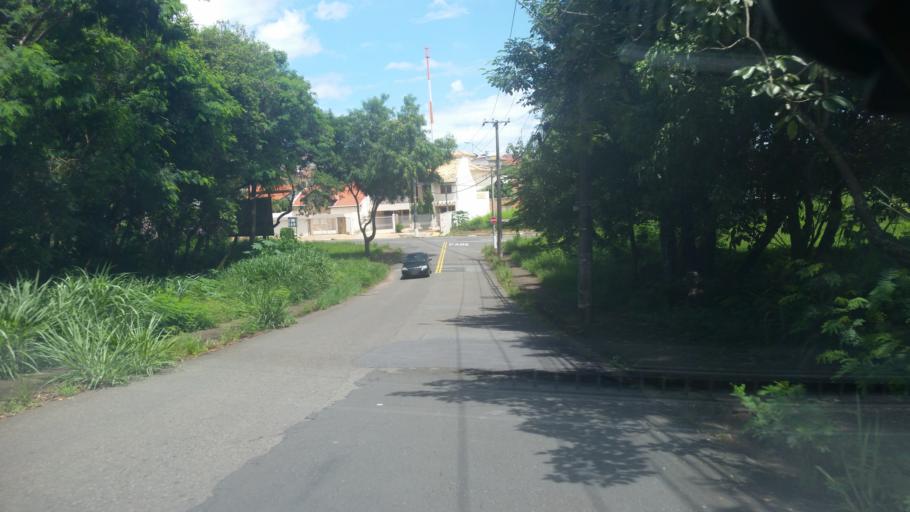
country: BR
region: Sao Paulo
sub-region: Campinas
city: Campinas
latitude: -22.8601
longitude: -47.0578
